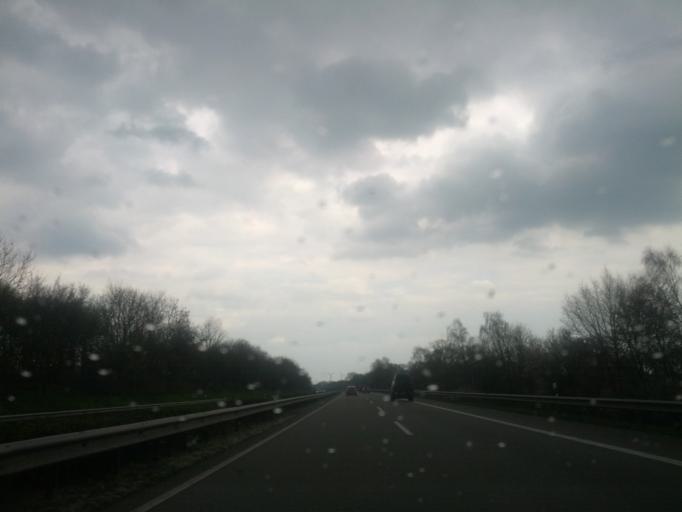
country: DE
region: Lower Saxony
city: Detern
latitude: 53.2485
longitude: 7.7154
